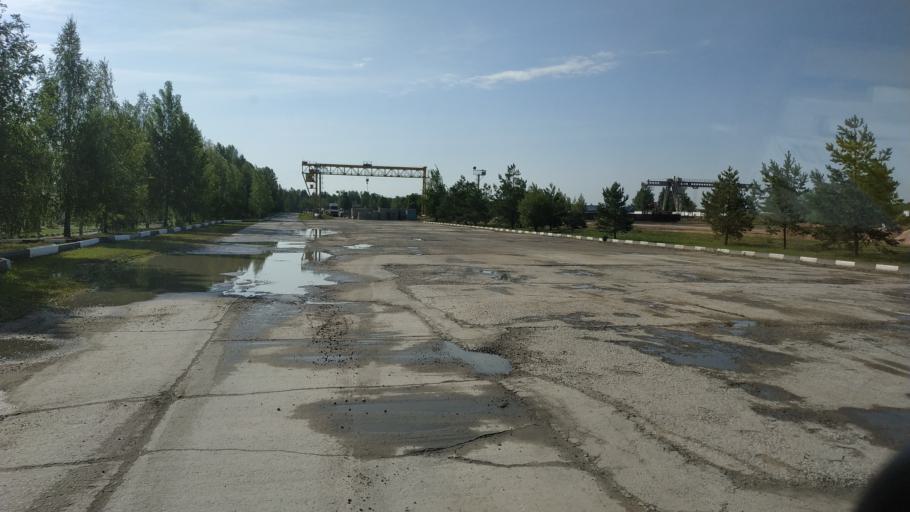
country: BY
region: Mogilev
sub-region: Mahilyowski Rayon
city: Veyno
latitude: 53.8409
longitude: 30.3829
